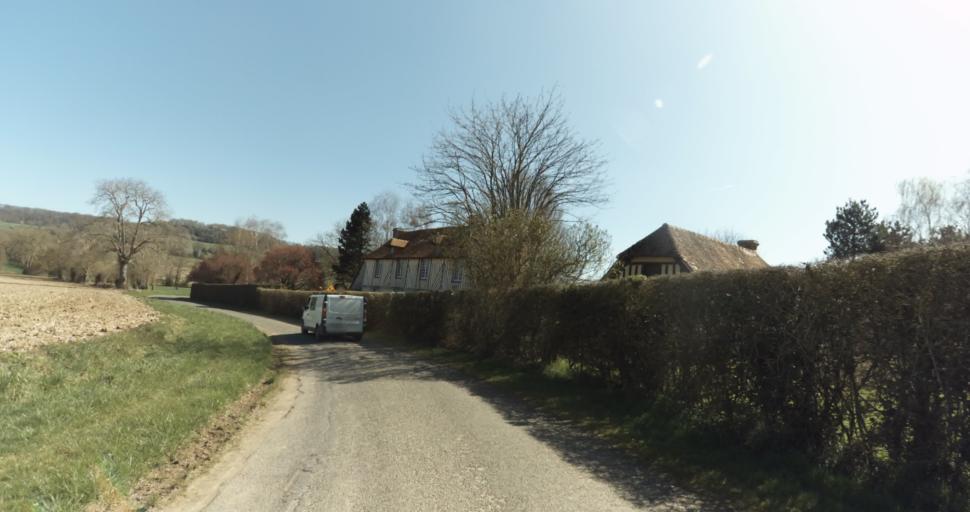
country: FR
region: Lower Normandy
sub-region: Departement du Calvados
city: Saint-Pierre-sur-Dives
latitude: 48.9935
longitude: 0.0262
